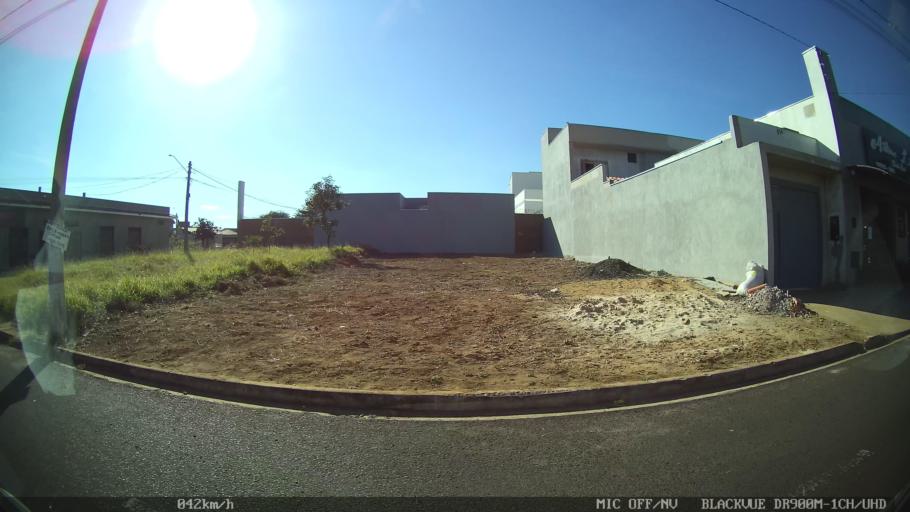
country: BR
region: Sao Paulo
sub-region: Franca
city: Franca
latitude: -20.5117
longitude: -47.4243
